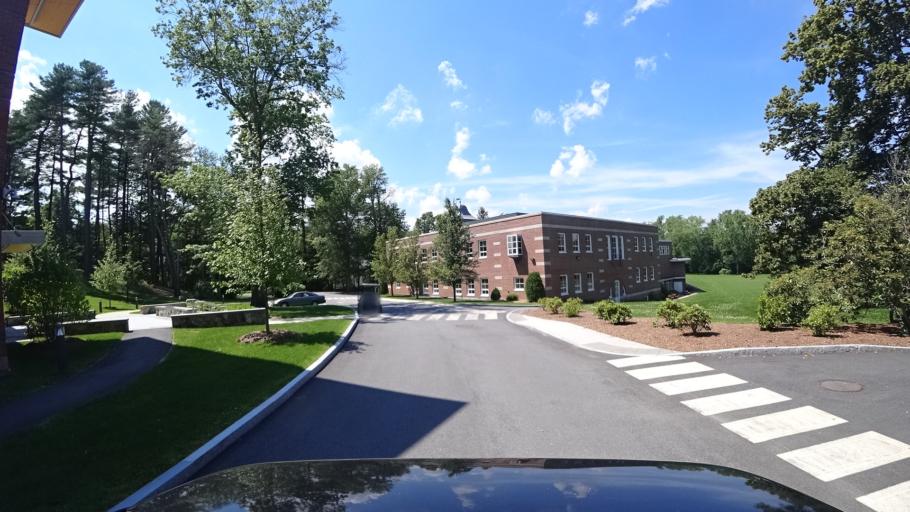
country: US
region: Massachusetts
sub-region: Norfolk County
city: Dedham
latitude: 42.2443
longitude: -71.1838
